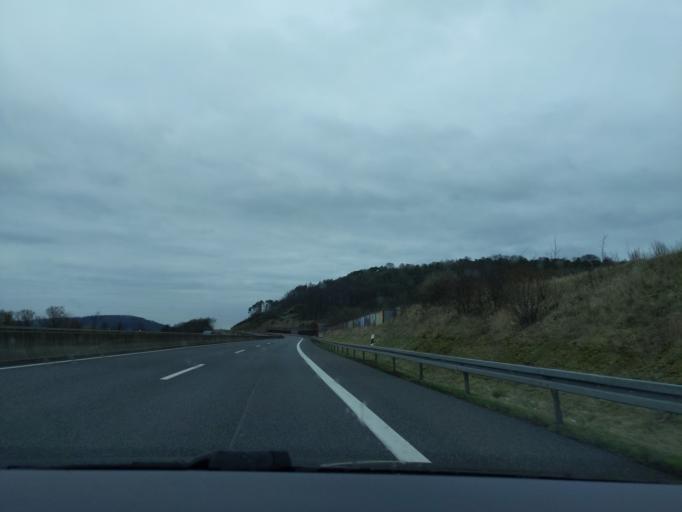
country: DE
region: Hesse
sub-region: Regierungsbezirk Giessen
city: Fronhausen
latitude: 50.7328
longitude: 8.7355
